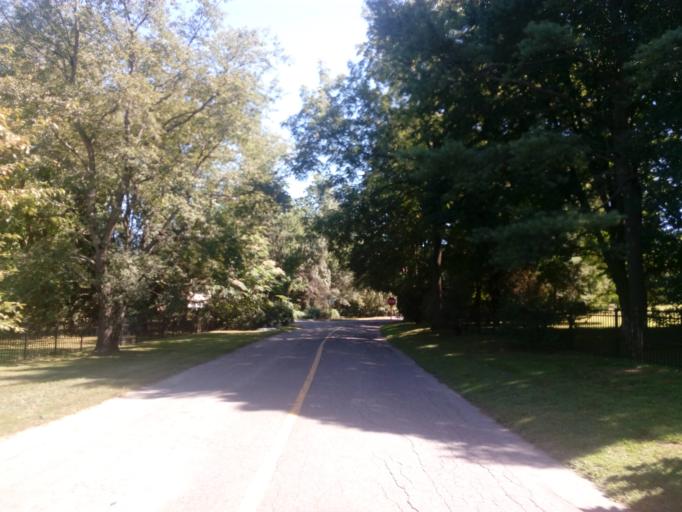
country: US
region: New York
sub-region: Nassau County
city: Upper Brookville
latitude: 40.8348
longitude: -73.5811
